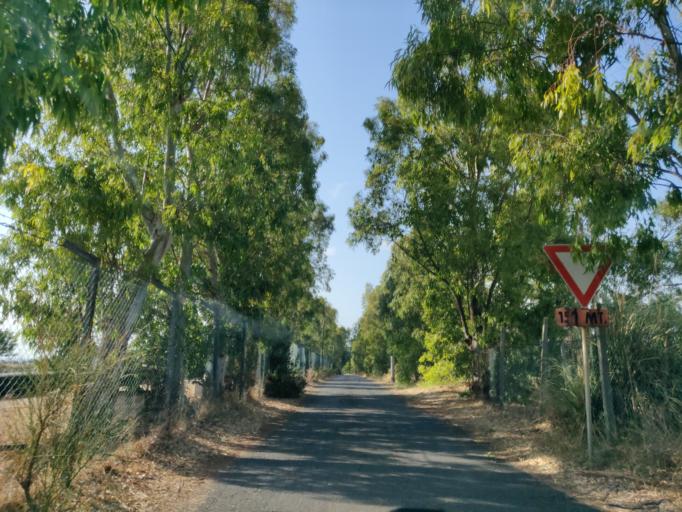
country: IT
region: Latium
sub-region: Citta metropolitana di Roma Capitale
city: Aurelia
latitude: 42.1353
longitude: 11.7616
